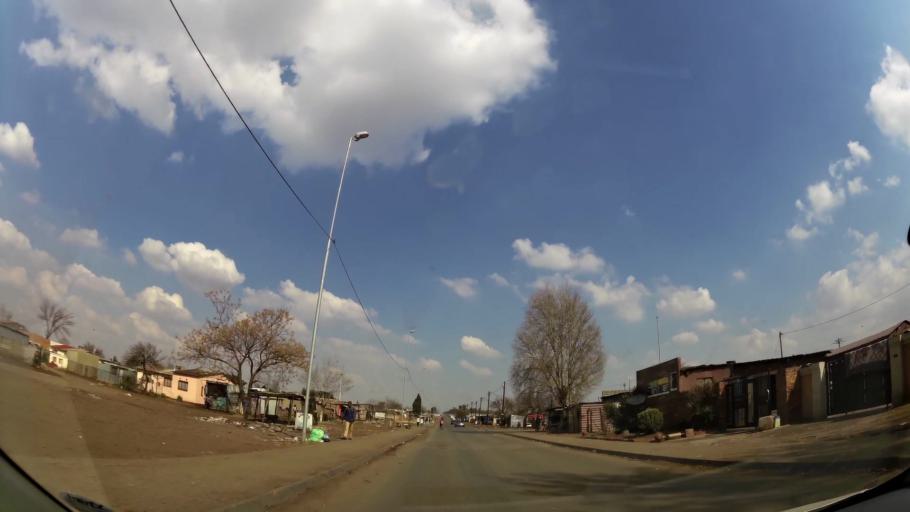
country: ZA
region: Gauteng
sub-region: Ekurhuleni Metropolitan Municipality
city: Germiston
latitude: -26.3048
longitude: 28.1496
